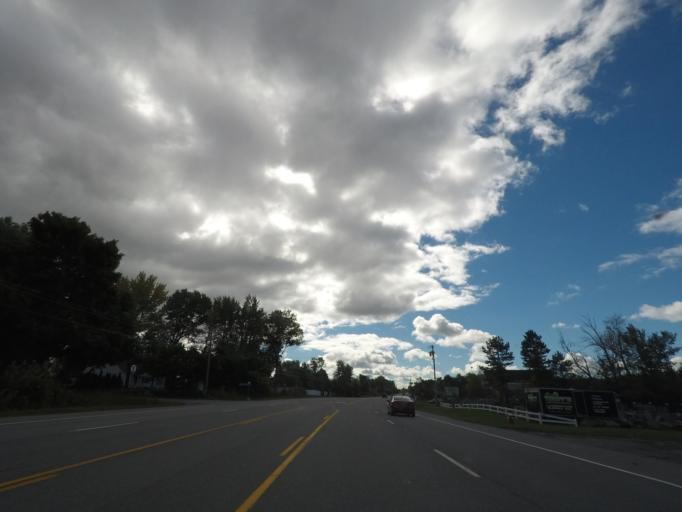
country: US
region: New York
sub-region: Albany County
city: Cohoes
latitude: 42.8019
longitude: -73.7335
